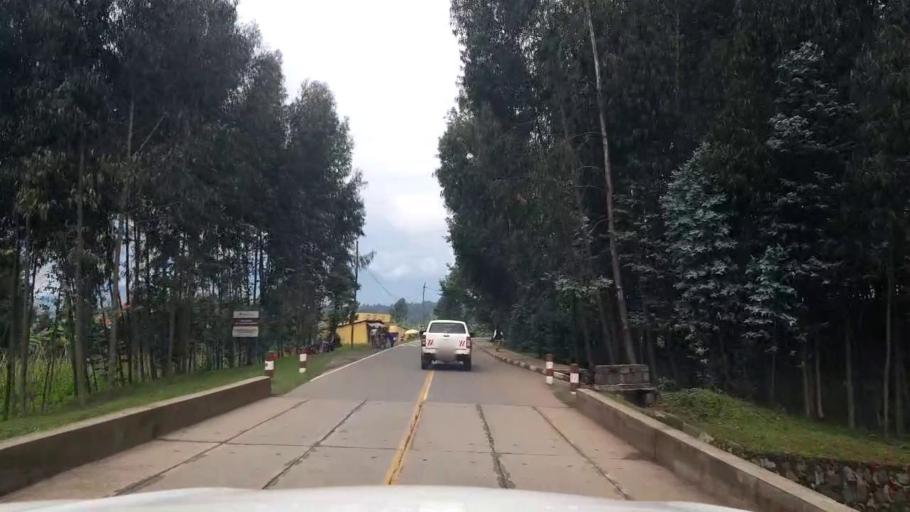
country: RW
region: Northern Province
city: Musanze
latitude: -1.4652
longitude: 29.6164
